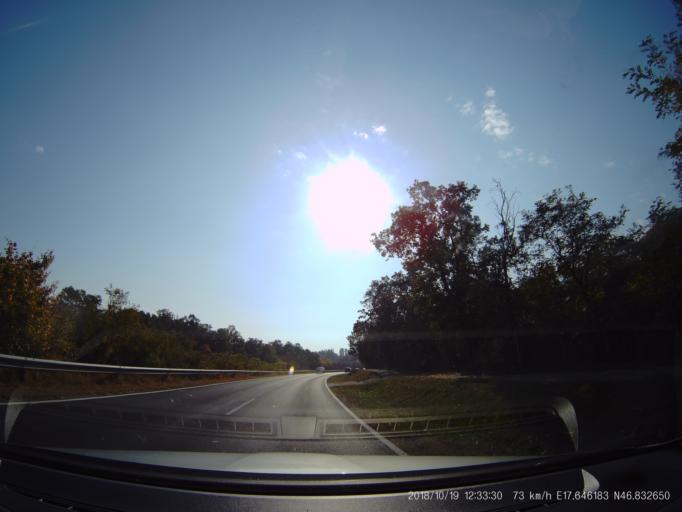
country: HU
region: Veszprem
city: Revfueloep
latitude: 46.8324
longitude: 17.6459
